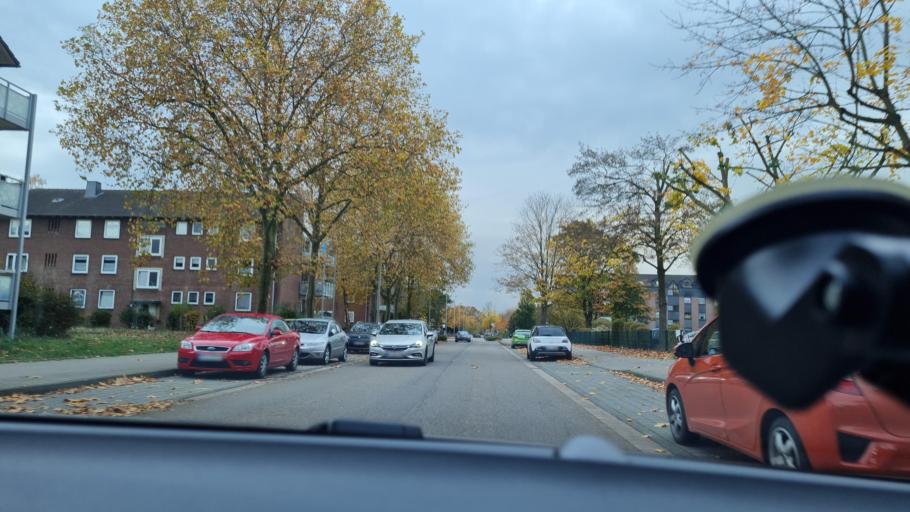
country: DE
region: North Rhine-Westphalia
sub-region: Regierungsbezirk Dusseldorf
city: Voerde
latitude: 51.6260
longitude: 6.6536
